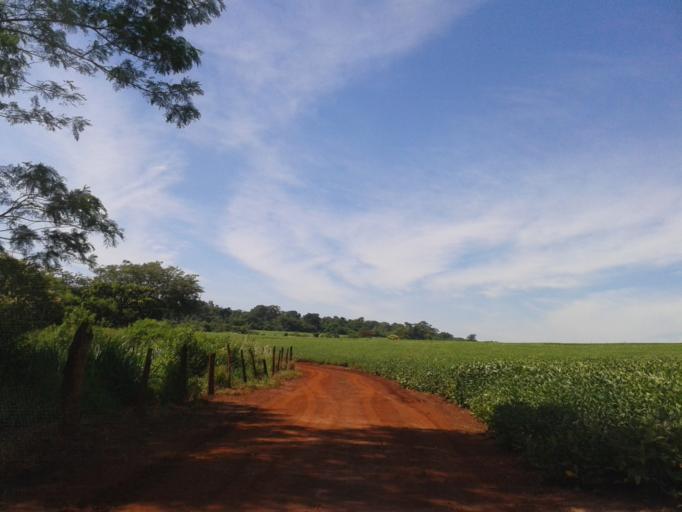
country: BR
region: Minas Gerais
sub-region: Capinopolis
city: Capinopolis
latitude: -18.6542
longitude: -49.7108
